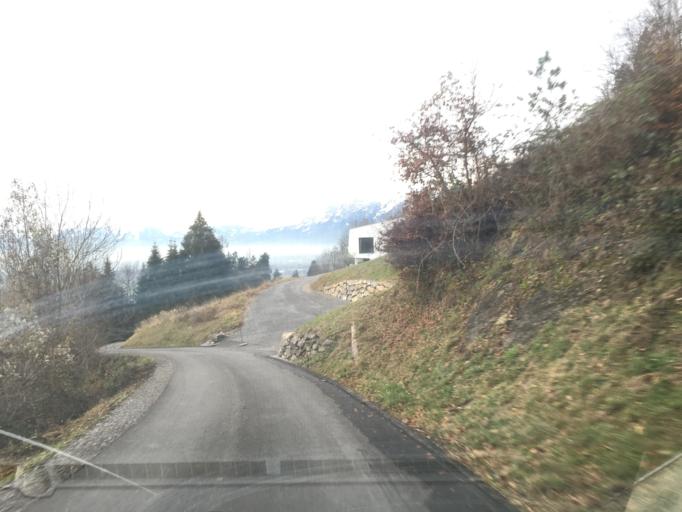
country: AT
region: Vorarlberg
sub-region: Politischer Bezirk Feldkirch
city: Klaus
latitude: 47.3141
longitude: 9.6550
